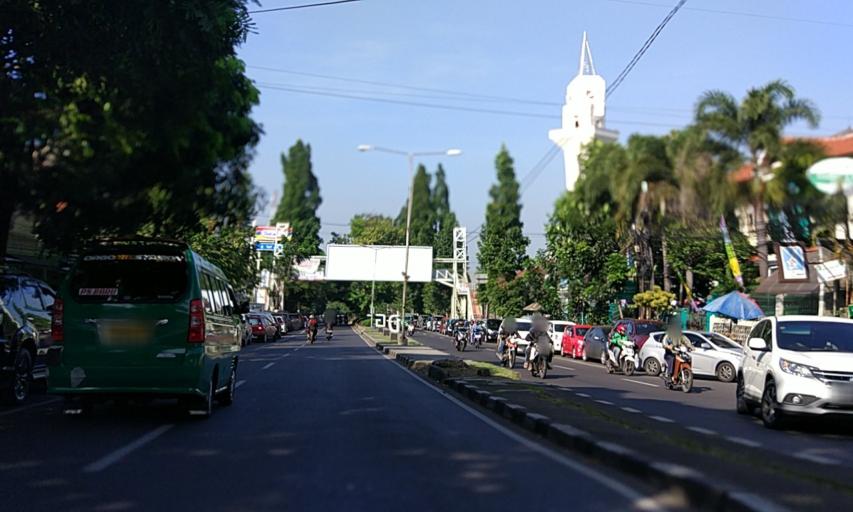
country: ID
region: West Java
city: Bandung
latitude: -6.8786
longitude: 107.6167
